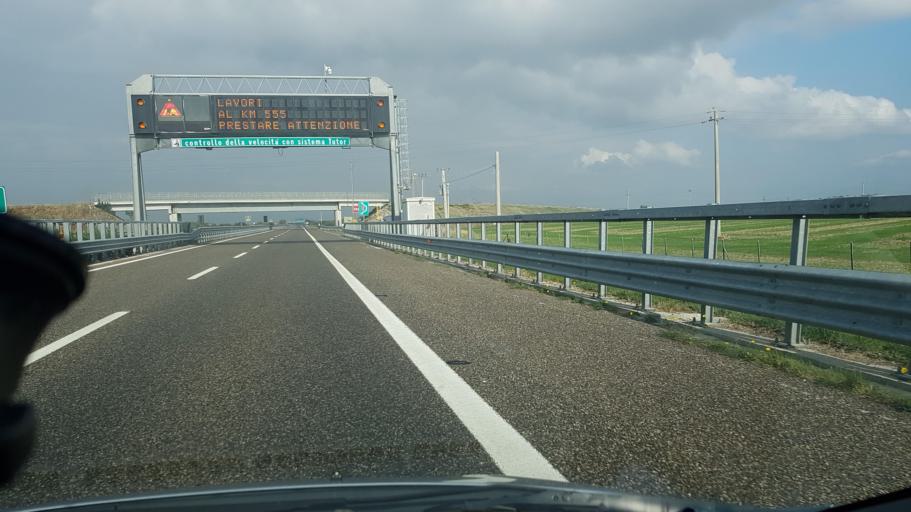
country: IT
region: Apulia
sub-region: Provincia di Foggia
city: Carapelle
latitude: 41.4127
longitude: 15.6678
